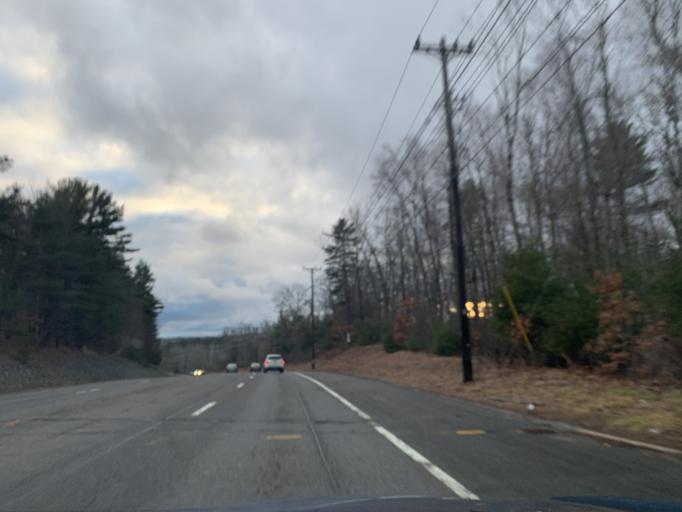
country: US
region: Massachusetts
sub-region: Norfolk County
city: Wrentham
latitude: 42.0707
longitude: -71.2908
